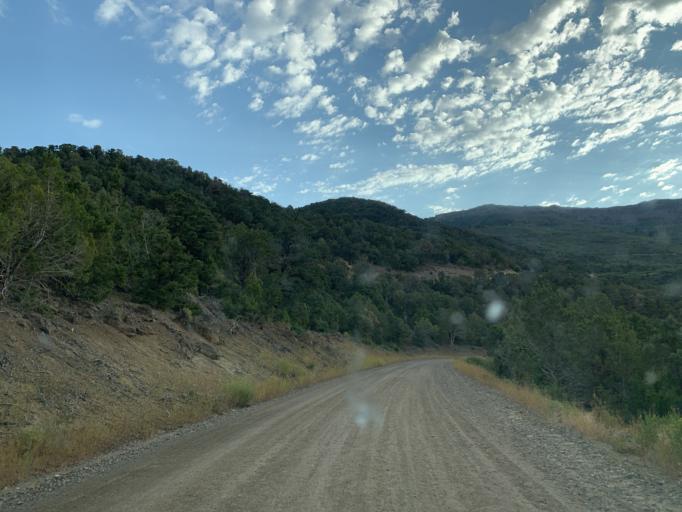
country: US
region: Colorado
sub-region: Mesa County
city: Palisade
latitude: 39.0085
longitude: -108.2462
